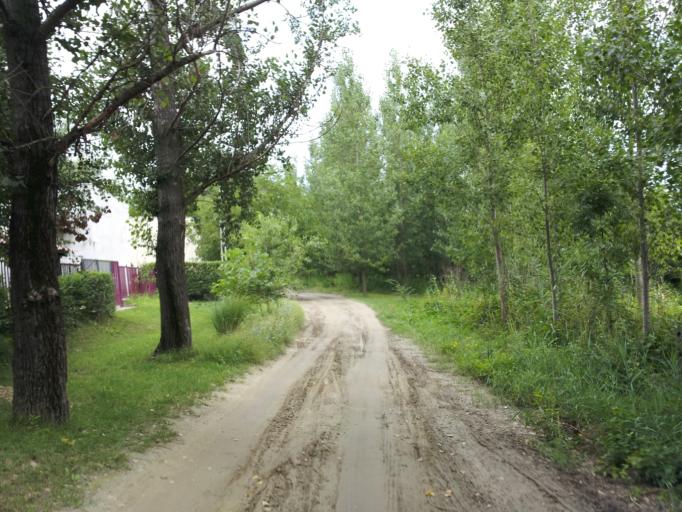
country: HU
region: Pest
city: Szigetcsep
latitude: 47.2238
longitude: 18.9696
